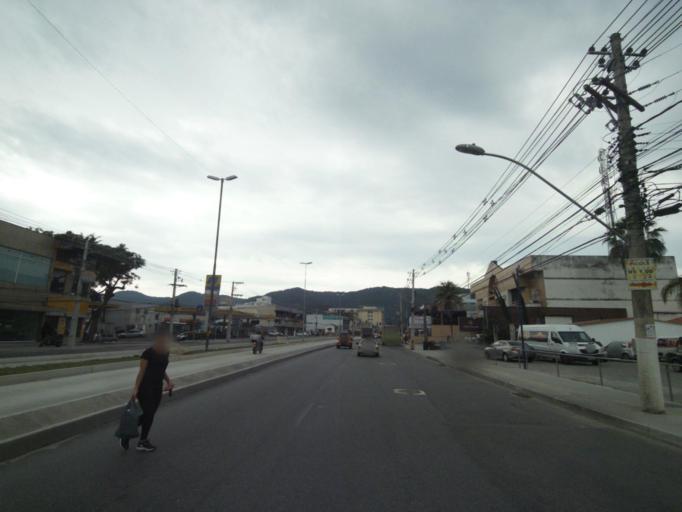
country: BR
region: Rio de Janeiro
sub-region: Niteroi
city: Niteroi
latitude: -22.9447
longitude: -43.0349
